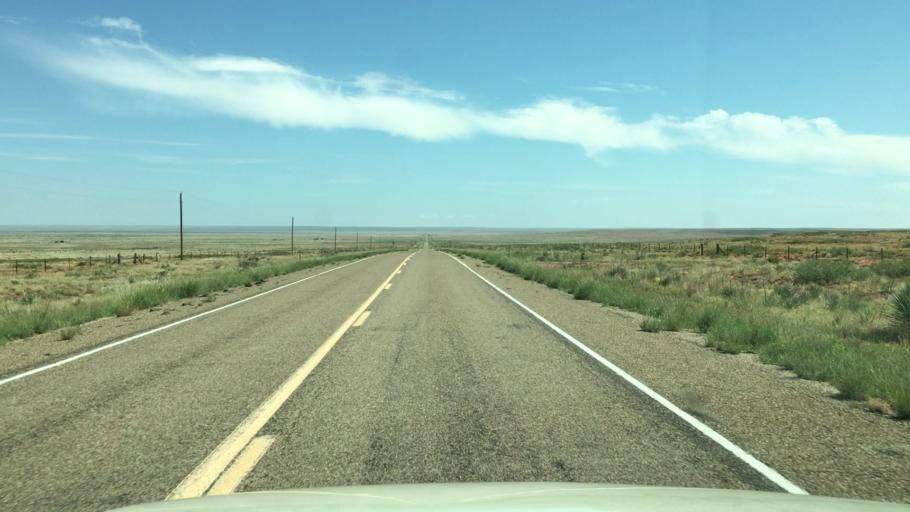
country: US
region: New Mexico
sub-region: Chaves County
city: Roswell
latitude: 33.9771
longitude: -104.5765
